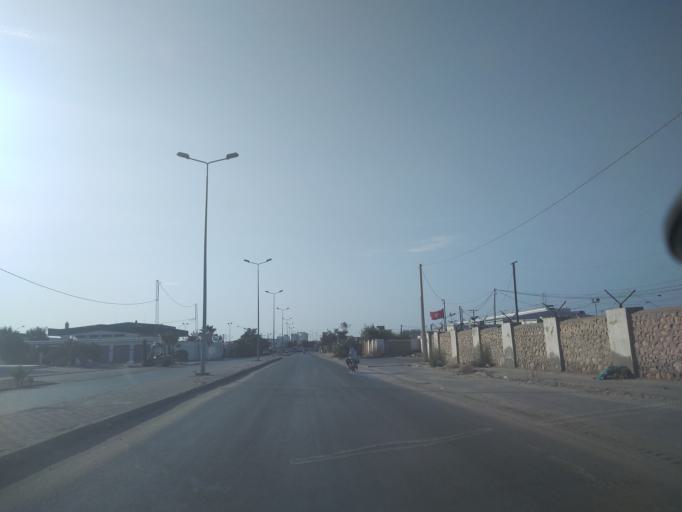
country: TN
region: Safaqis
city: Sfax
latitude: 34.7233
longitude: 10.7586
